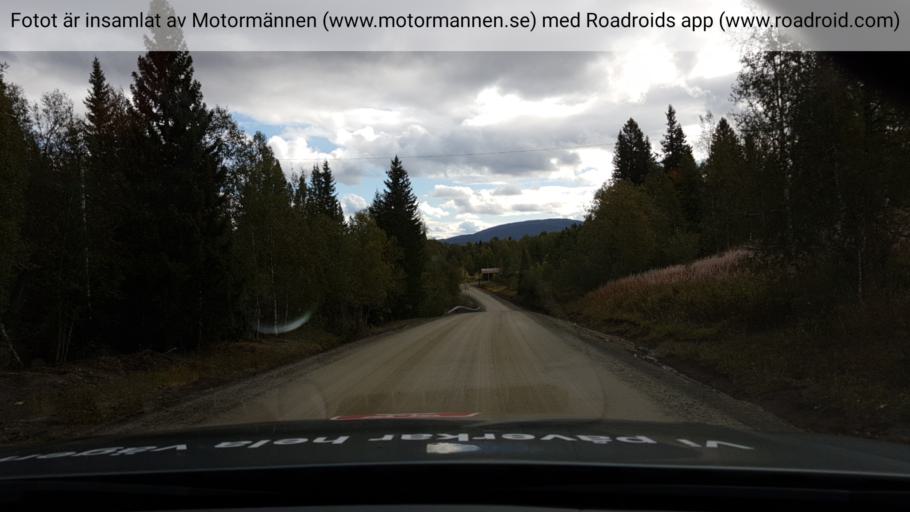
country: SE
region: Jaemtland
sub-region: Are Kommun
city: Are
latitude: 63.7139
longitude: 12.6258
